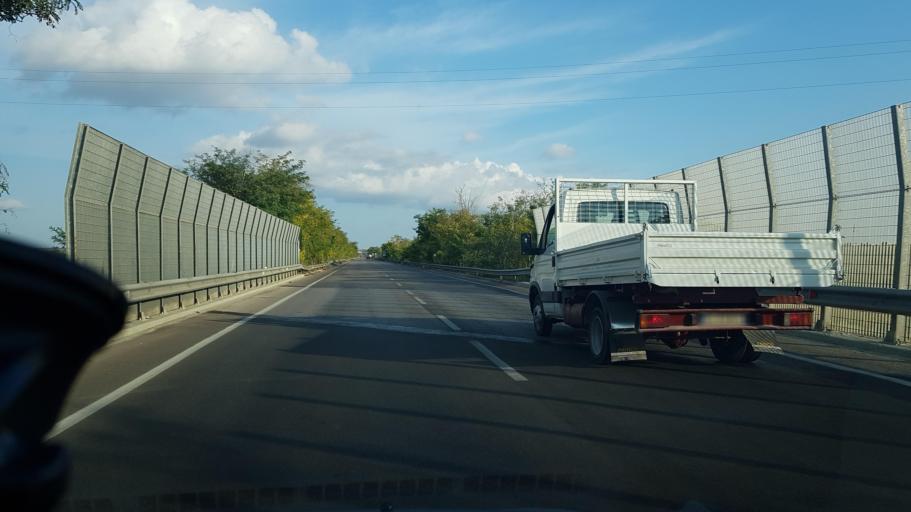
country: IT
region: Apulia
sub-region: Provincia di Lecce
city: Felline
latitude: 39.9510
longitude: 18.1427
